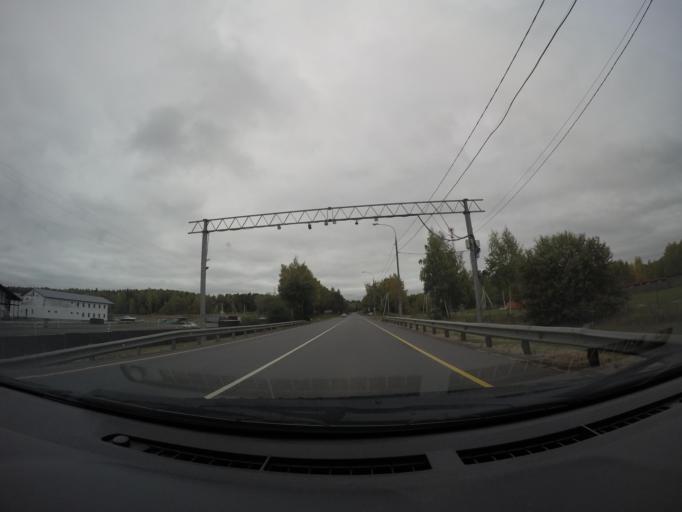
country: RU
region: Moskovskaya
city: Ruza
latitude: 55.7582
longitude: 36.2600
